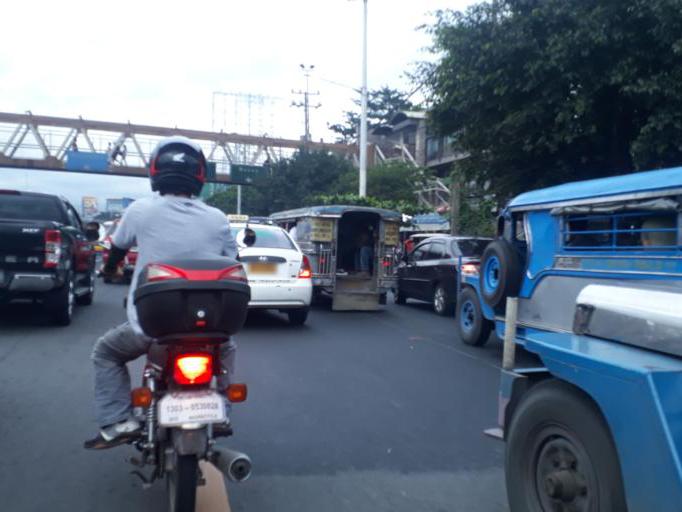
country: PH
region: Metro Manila
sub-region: Quezon City
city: Quezon City
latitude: 14.6715
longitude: 121.0790
